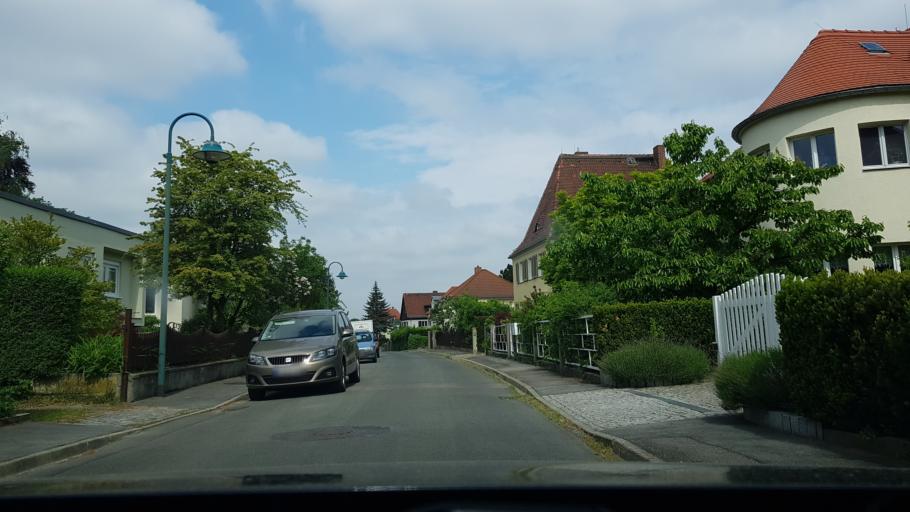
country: DE
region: Saxony
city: Bannewitz
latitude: 51.0289
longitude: 13.6958
